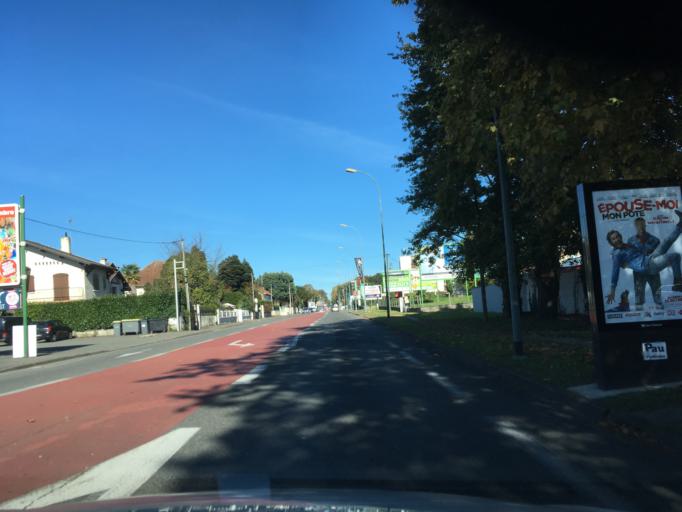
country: FR
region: Aquitaine
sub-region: Departement des Pyrenees-Atlantiques
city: Lons
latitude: 43.3299
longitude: -0.3796
